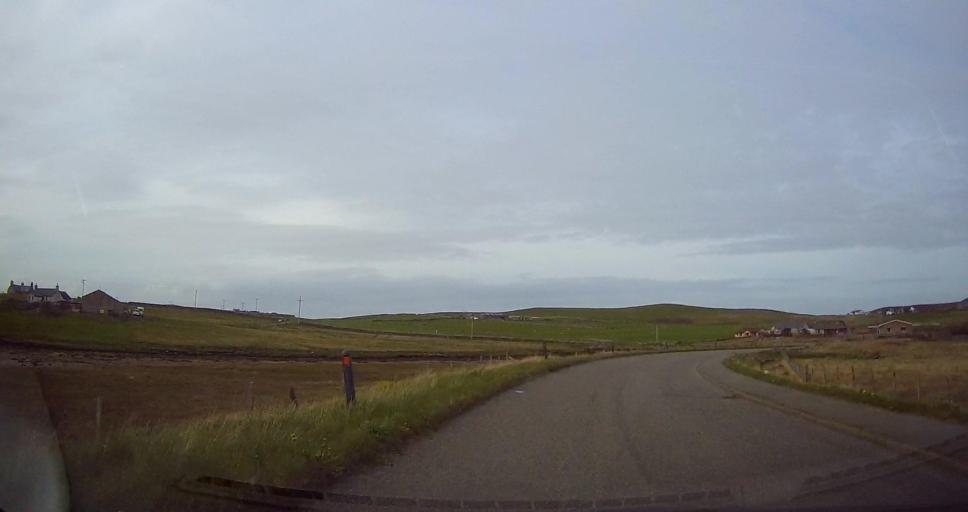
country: GB
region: Scotland
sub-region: Shetland Islands
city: Shetland
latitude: 60.1558
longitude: -1.1157
